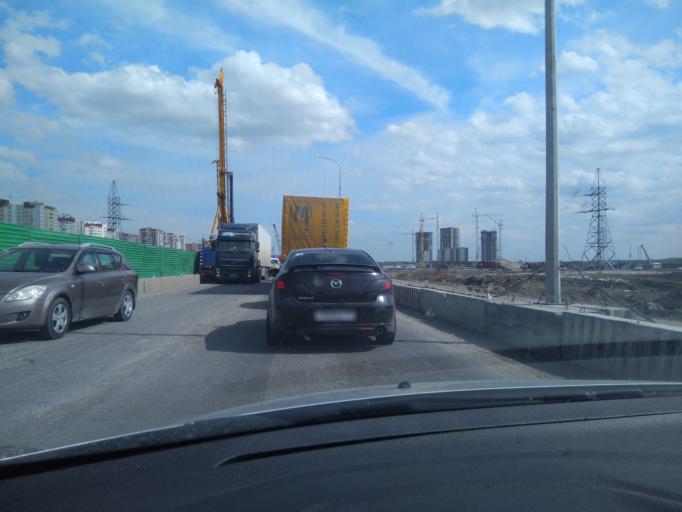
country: RU
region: Tjumen
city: Tyumen
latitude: 57.1059
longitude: 65.5591
